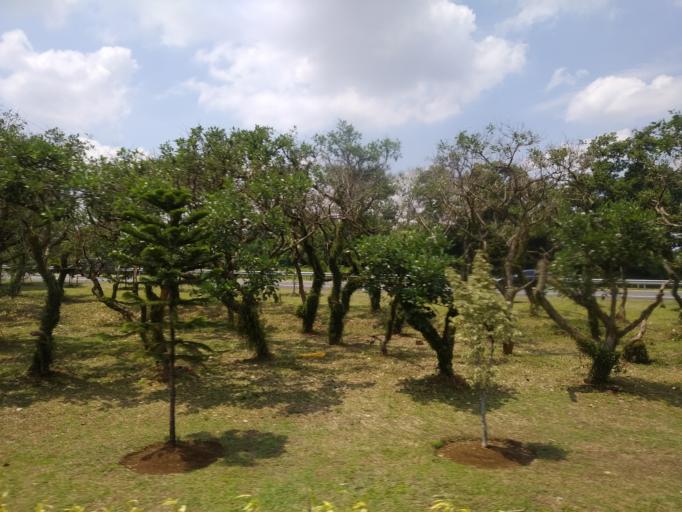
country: ID
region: West Java
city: Bogor
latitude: -6.5936
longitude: 106.8339
